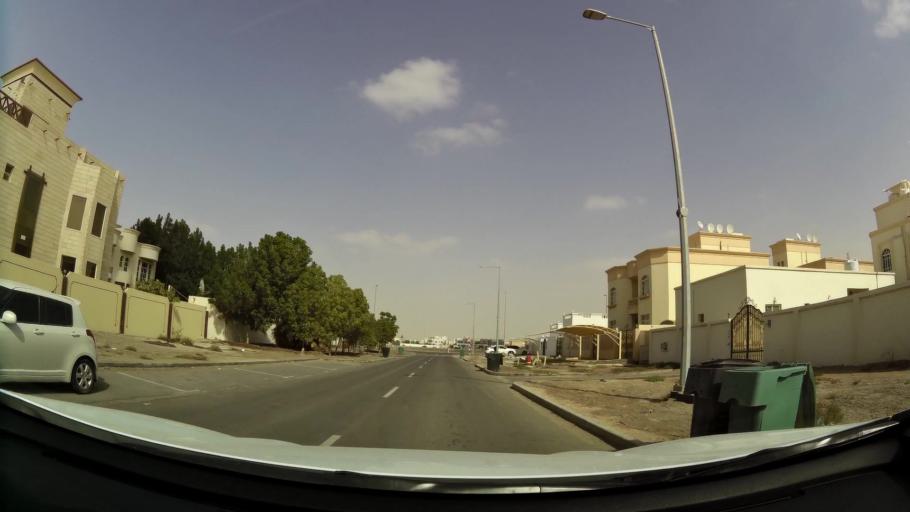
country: AE
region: Abu Dhabi
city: Abu Dhabi
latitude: 24.4253
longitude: 54.5612
